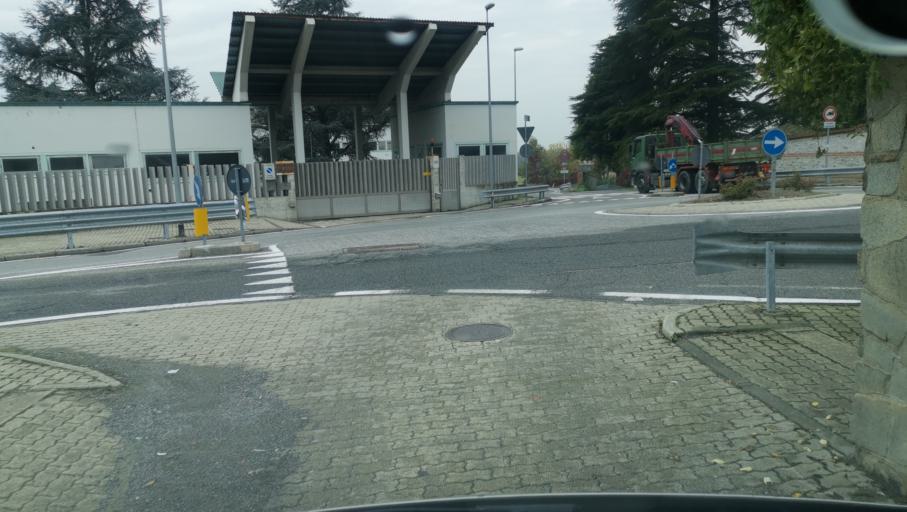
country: IT
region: Piedmont
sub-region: Provincia di Torino
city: Gassino Torinese
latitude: 45.1240
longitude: 7.8188
